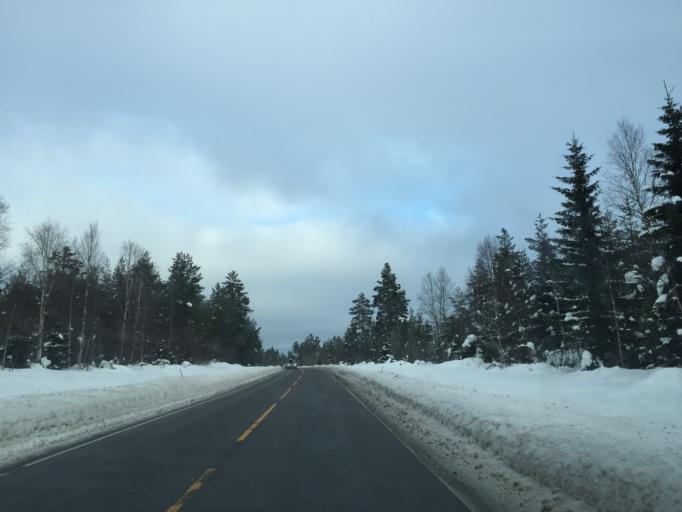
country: NO
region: Hedmark
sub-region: Trysil
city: Innbygda
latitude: 61.1416
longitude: 12.1202
